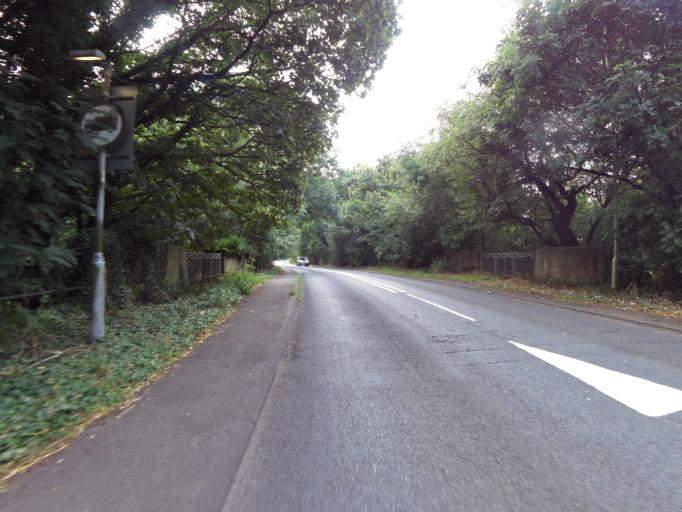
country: GB
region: England
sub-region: Hertfordshire
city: Shenley AV
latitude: 51.7156
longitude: -0.2998
